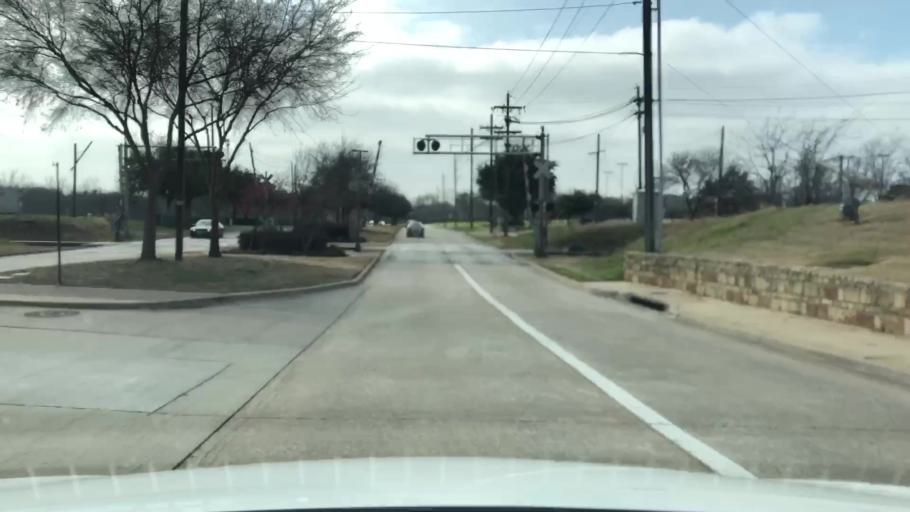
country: US
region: Texas
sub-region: Dallas County
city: Addison
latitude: 33.0218
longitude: -96.8538
